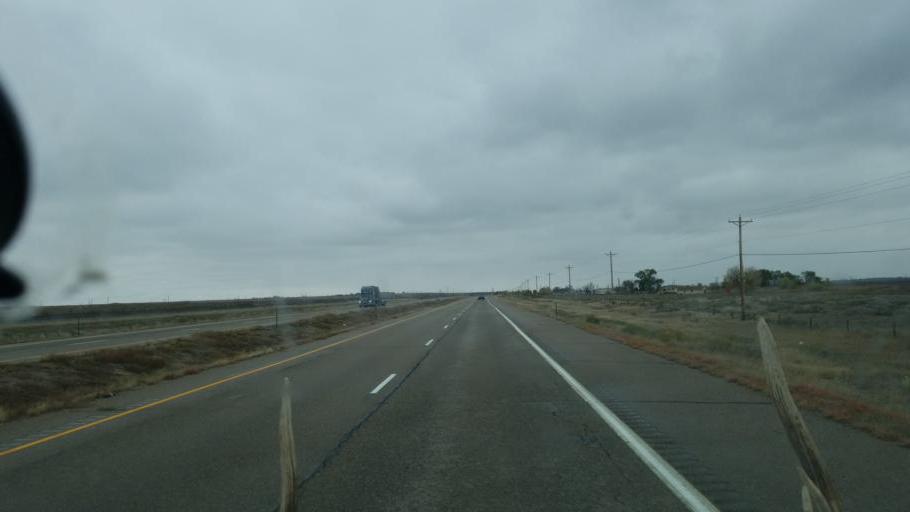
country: US
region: Colorado
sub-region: Pueblo County
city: Pueblo
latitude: 38.2708
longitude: -104.4153
